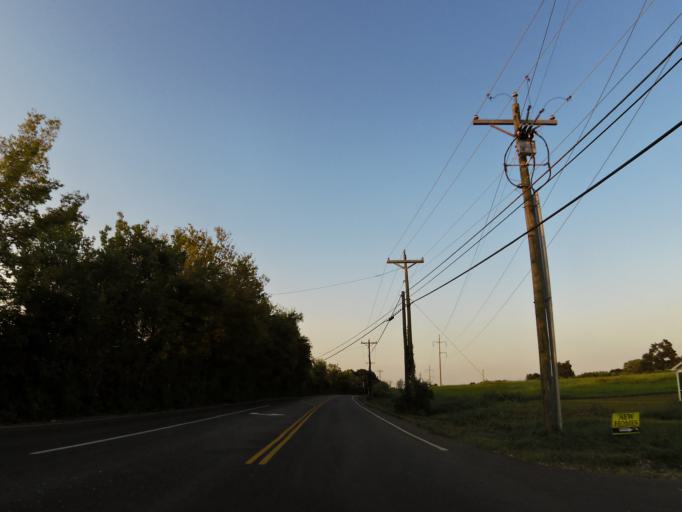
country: US
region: Tennessee
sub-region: Loudon County
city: Loudon
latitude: 35.7042
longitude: -84.3724
